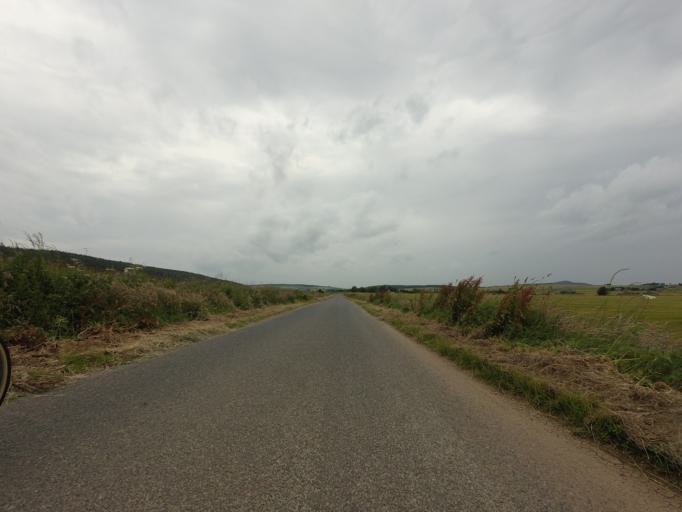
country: GB
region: Scotland
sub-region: Aberdeenshire
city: Portsoy
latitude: 57.6642
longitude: -2.7332
